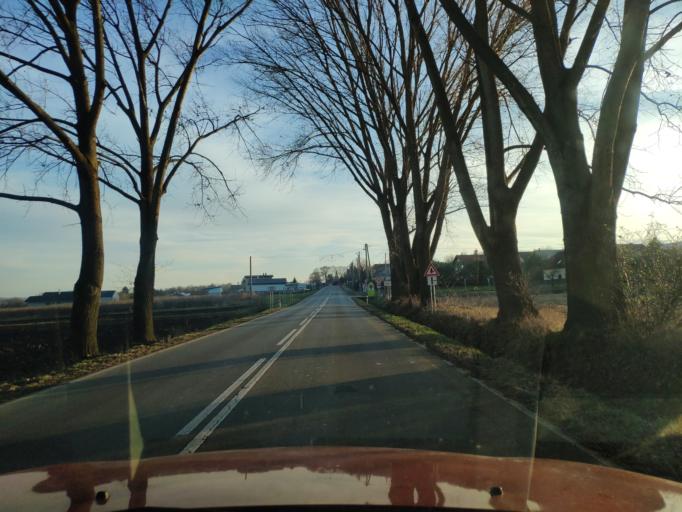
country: SK
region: Kosicky
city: Kosice
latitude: 48.8064
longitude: 21.3015
